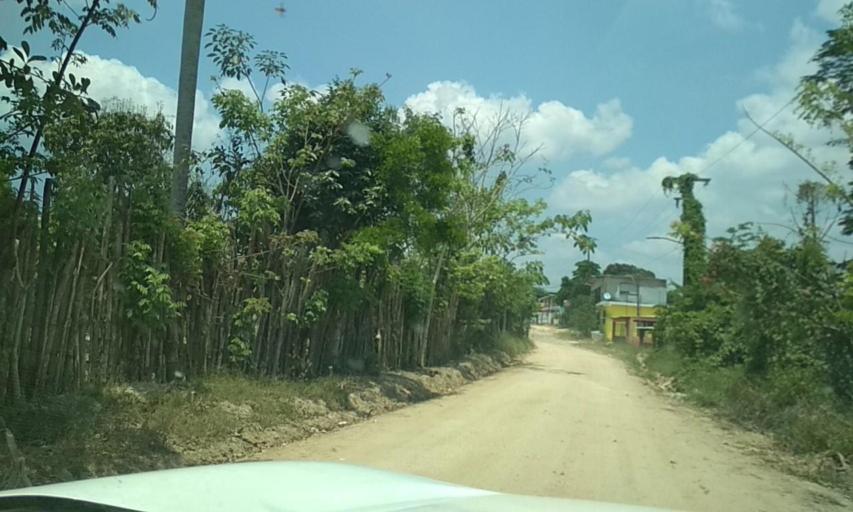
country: MX
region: Veracruz
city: Las Choapas
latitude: 17.9165
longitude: -94.0893
